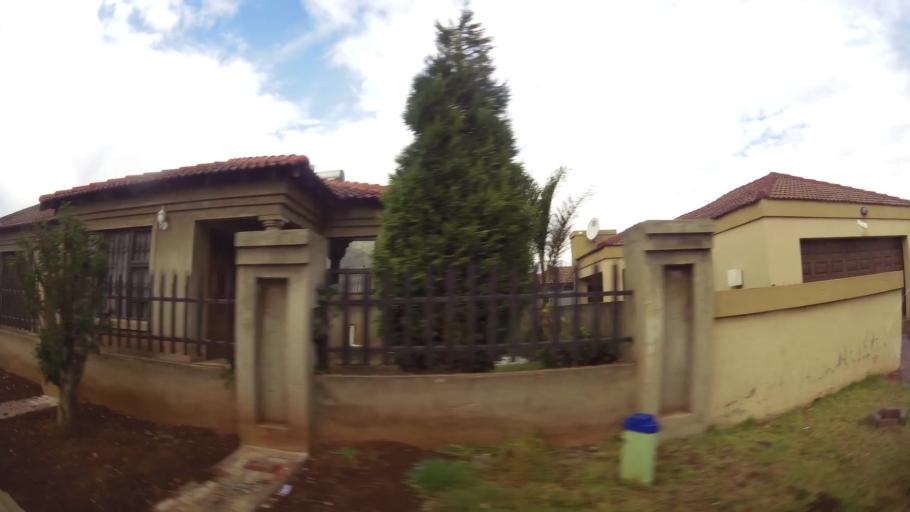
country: ZA
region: Gauteng
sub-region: Ekurhuleni Metropolitan Municipality
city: Germiston
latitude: -26.3296
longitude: 28.1927
